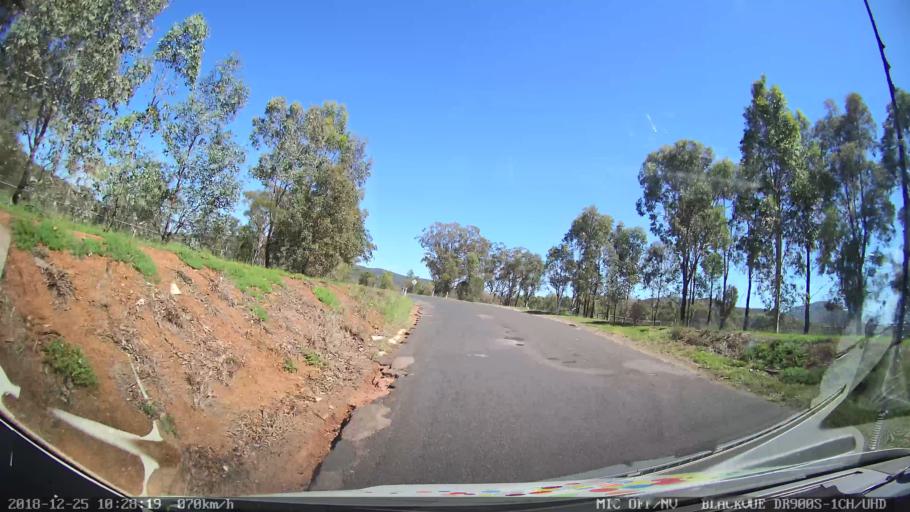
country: AU
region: New South Wales
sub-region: Muswellbrook
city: Denman
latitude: -32.3827
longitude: 150.4651
